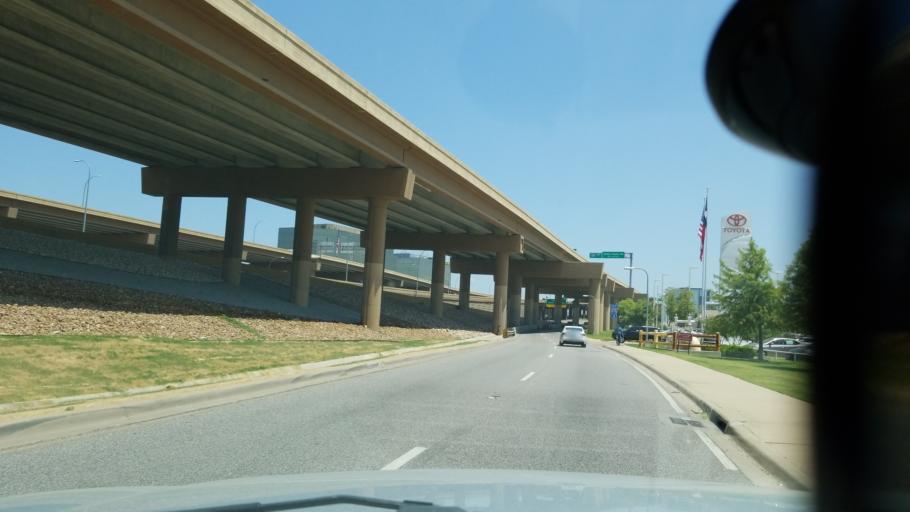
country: US
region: Texas
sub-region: Dallas County
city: Farmers Branch
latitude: 32.9084
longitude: -96.8907
